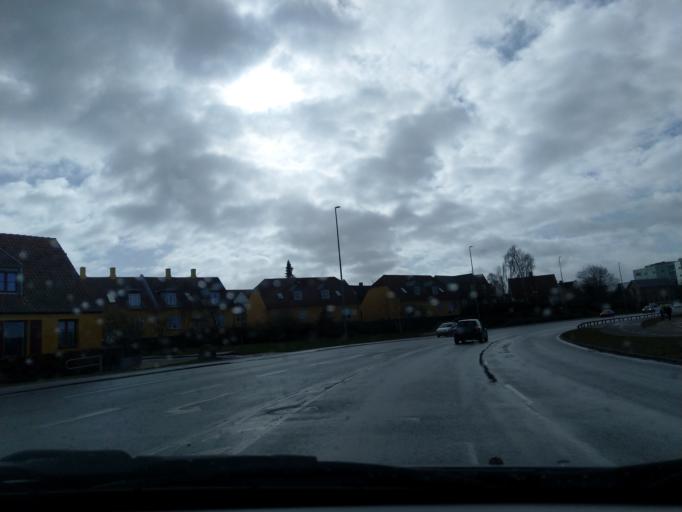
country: DK
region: Zealand
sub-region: Naestved Kommune
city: Naestved
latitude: 55.2272
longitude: 11.7577
